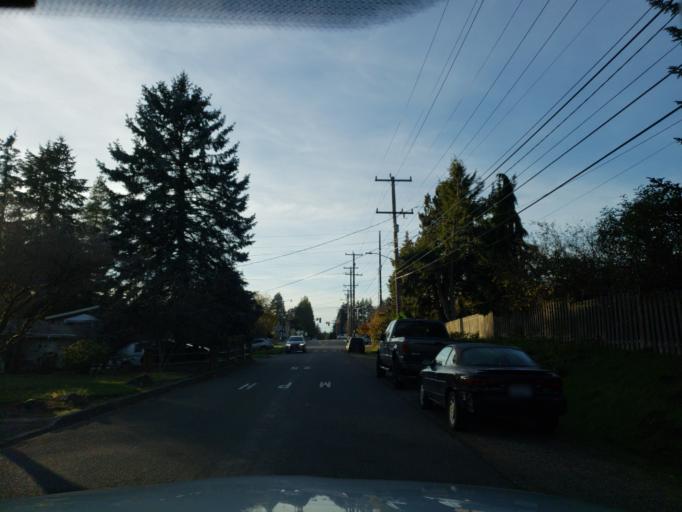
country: US
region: Washington
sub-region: King County
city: Shoreline
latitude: 47.7487
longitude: -122.3430
